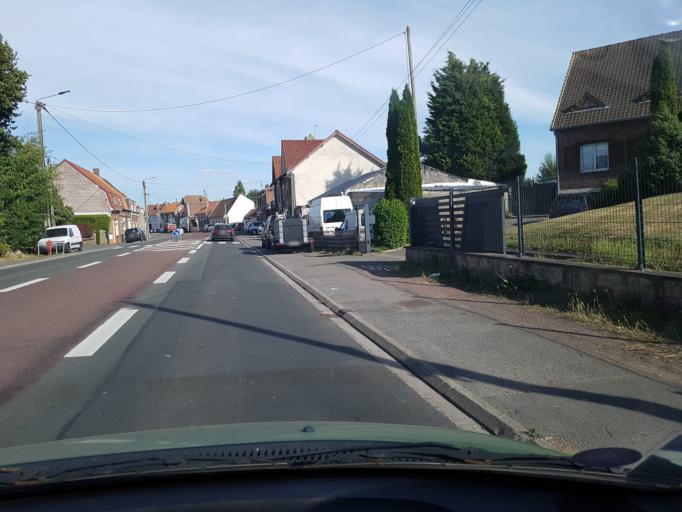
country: FR
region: Nord-Pas-de-Calais
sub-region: Departement du Pas-de-Calais
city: Vendin-les-Bethune
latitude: 50.5403
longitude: 2.6097
